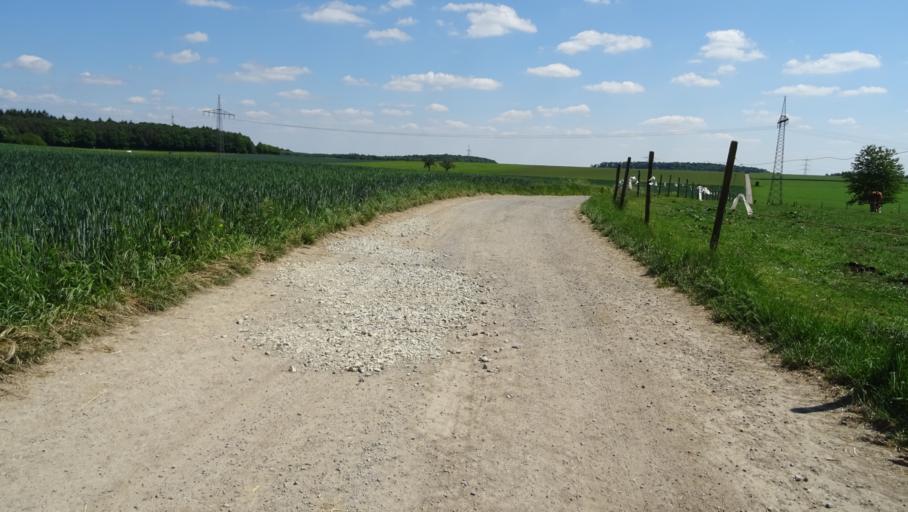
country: DE
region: Baden-Wuerttemberg
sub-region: Karlsruhe Region
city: Buchen
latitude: 49.5031
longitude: 9.3427
